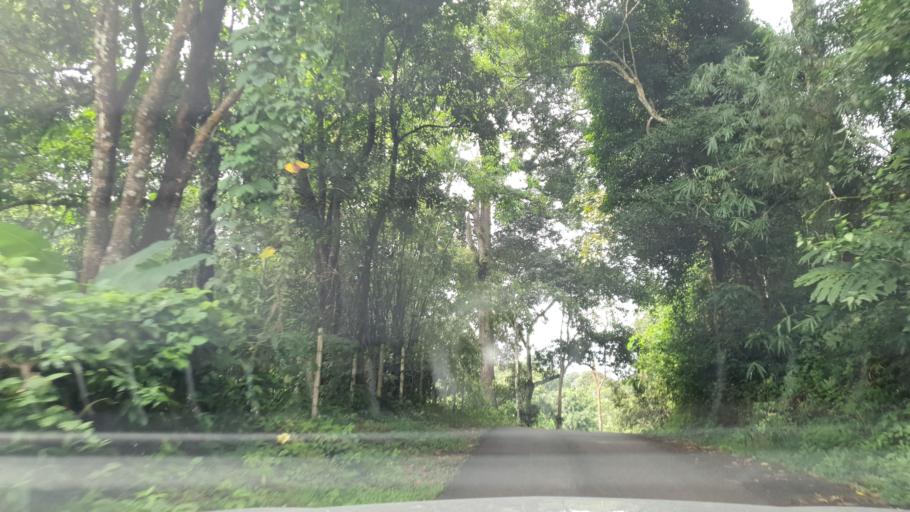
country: TH
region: Chiang Mai
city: Mae On
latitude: 18.9344
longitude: 99.3111
